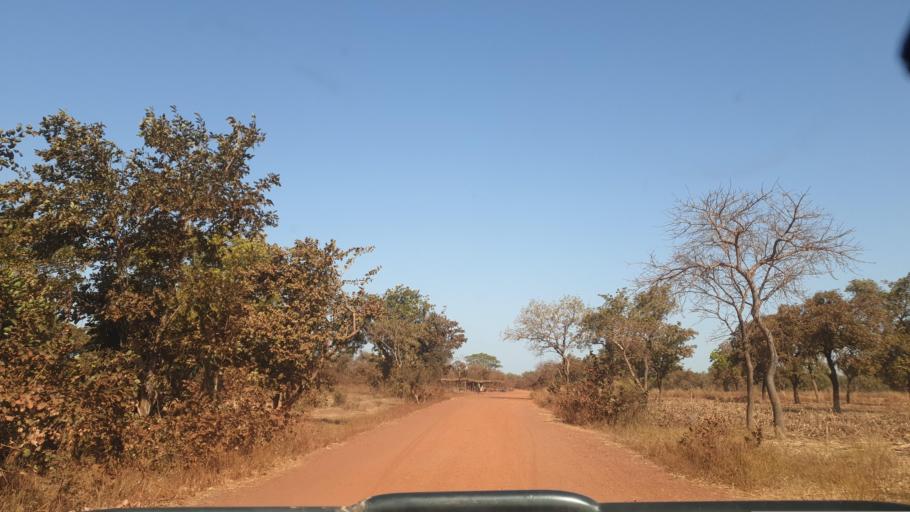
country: ML
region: Sikasso
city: Bougouni
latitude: 11.8462
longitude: -6.9786
